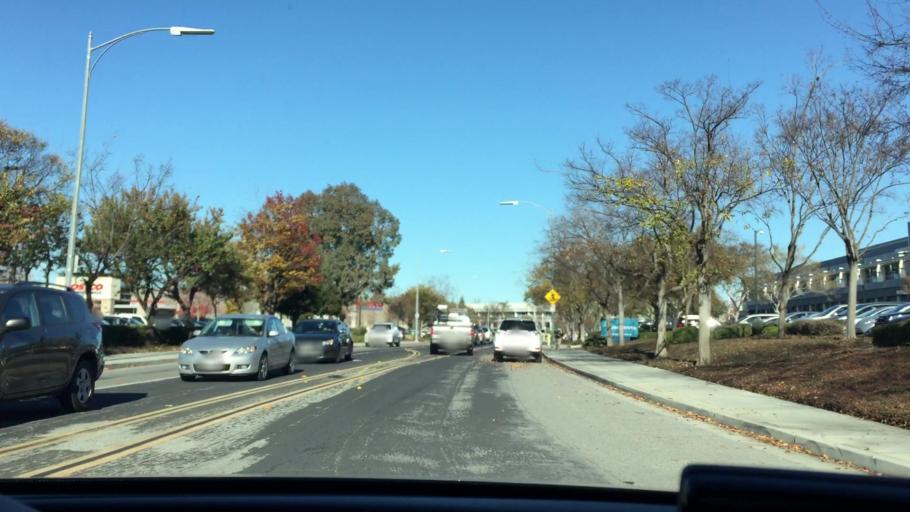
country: US
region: California
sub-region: Santa Clara County
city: Milpitas
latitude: 37.3886
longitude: -121.8829
